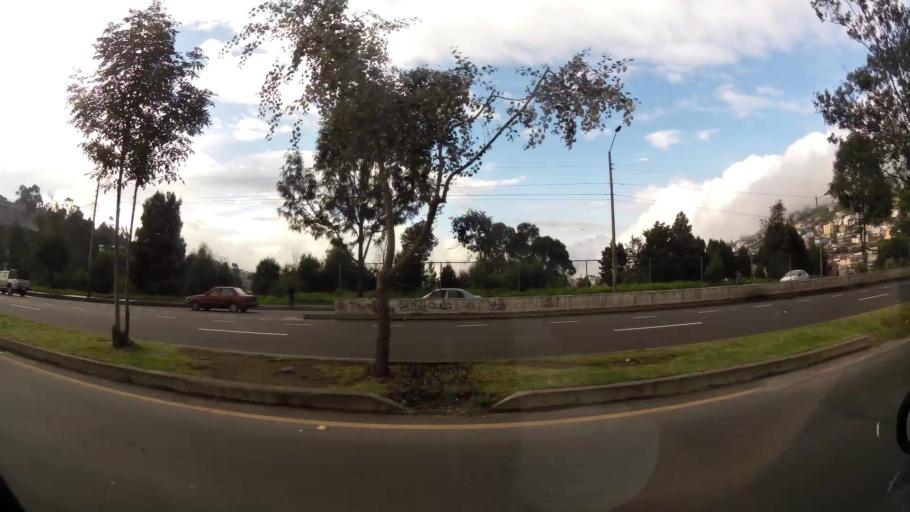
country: EC
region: Pichincha
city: Quito
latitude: -0.2372
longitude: -78.4864
